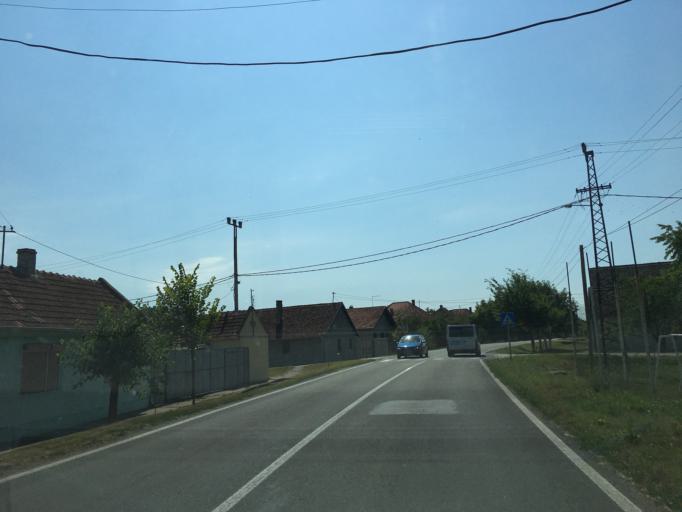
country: RS
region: Central Serbia
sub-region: Belgrade
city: Grocka
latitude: 44.7537
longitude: 20.7462
